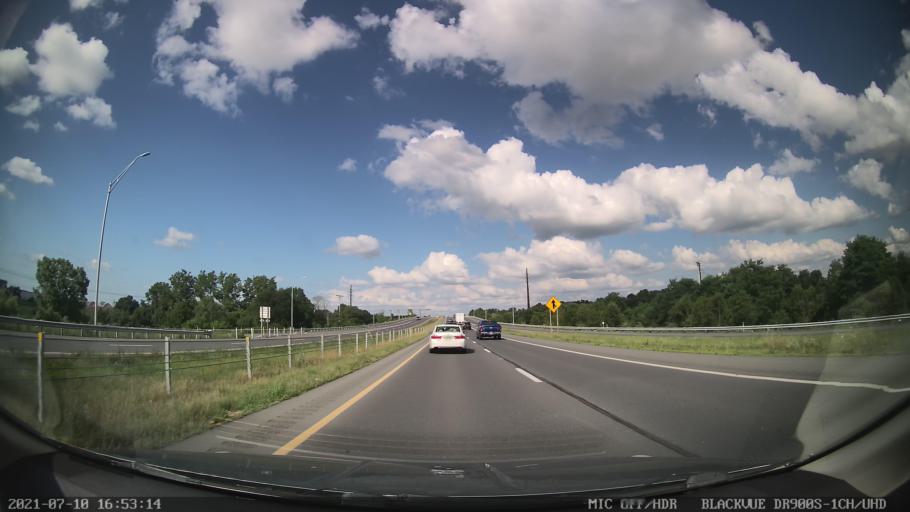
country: US
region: Pennsylvania
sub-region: Lehigh County
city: Trexlertown
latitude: 40.5594
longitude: -75.6070
